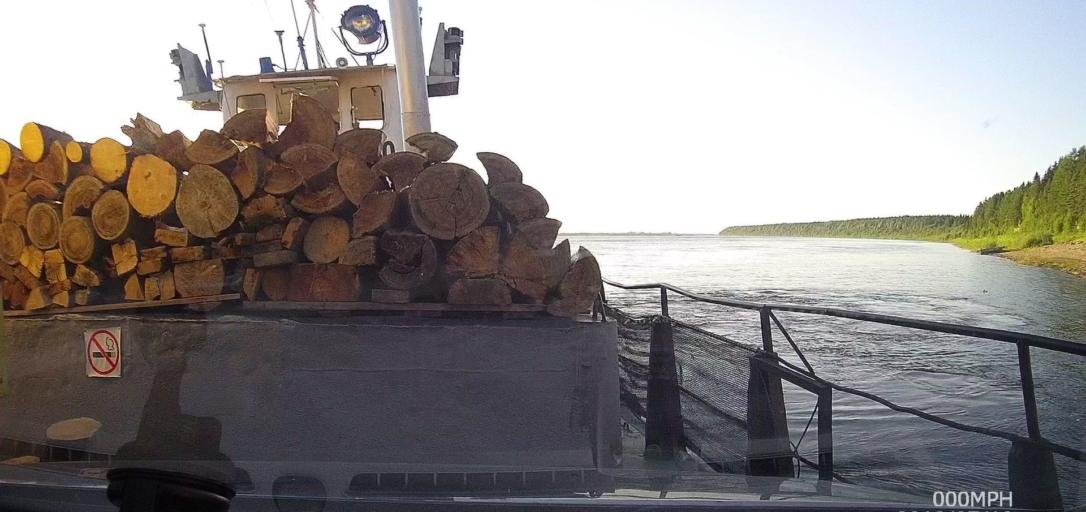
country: RU
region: Arkhangelskaya
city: Lukovetskiy
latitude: 64.1571
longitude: 41.9203
